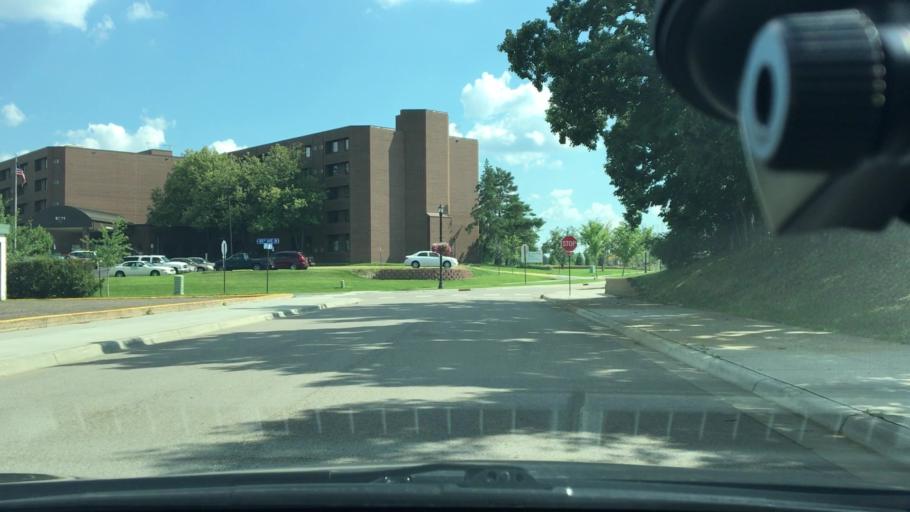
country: US
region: Minnesota
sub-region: Hennepin County
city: New Hope
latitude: 45.0369
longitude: -93.3849
